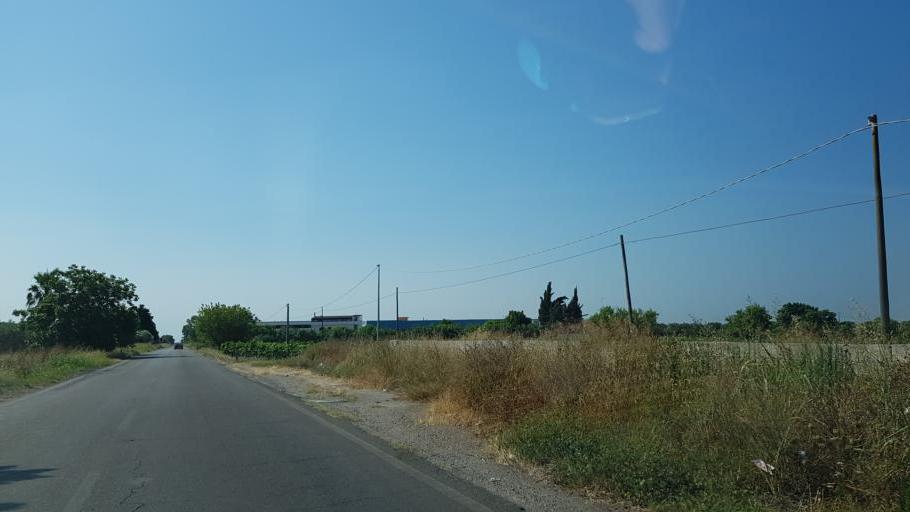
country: IT
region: Apulia
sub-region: Provincia di Brindisi
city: San Donaci
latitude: 40.4375
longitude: 17.9333
